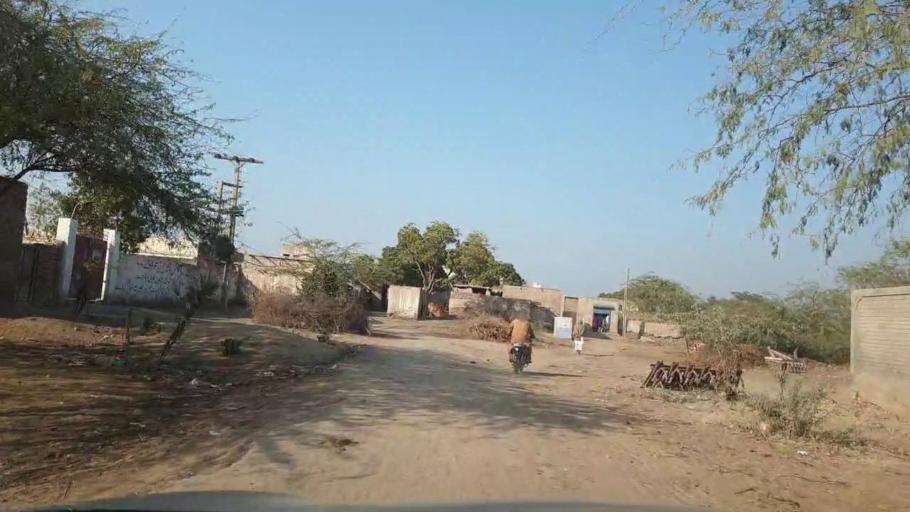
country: PK
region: Sindh
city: Tando Allahyar
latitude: 25.5159
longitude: 68.8460
